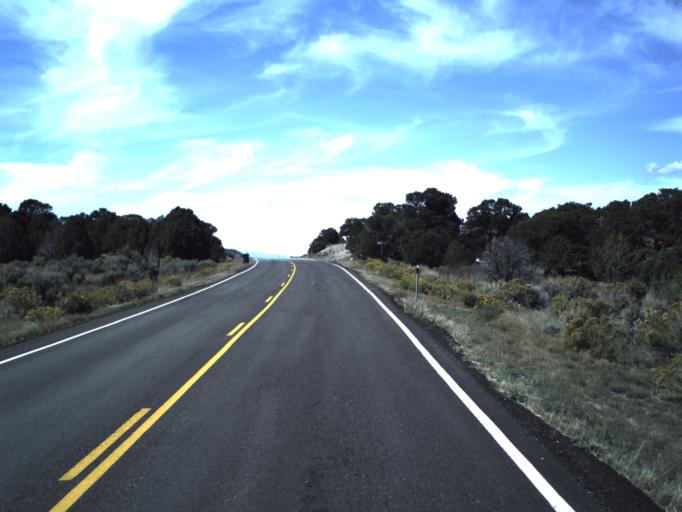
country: US
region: Utah
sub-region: Wayne County
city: Loa
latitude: 38.2329
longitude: -111.3635
